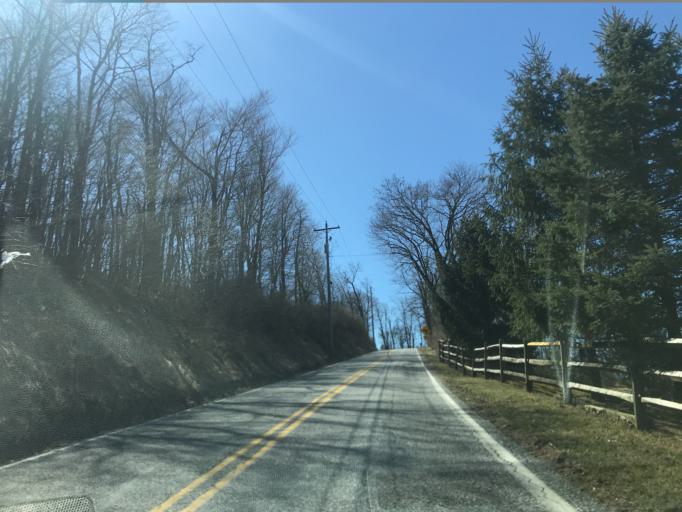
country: US
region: Pennsylvania
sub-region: York County
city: Shrewsbury
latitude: 39.7618
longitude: -76.6519
